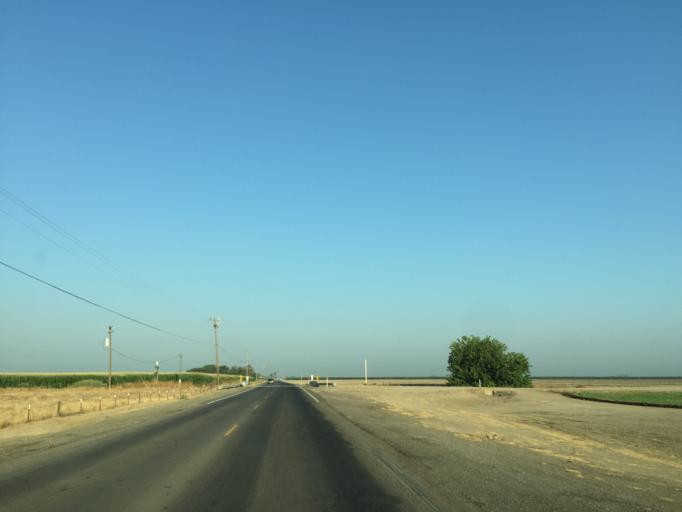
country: US
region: California
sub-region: Tulare County
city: Cutler
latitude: 36.4583
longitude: -119.3482
